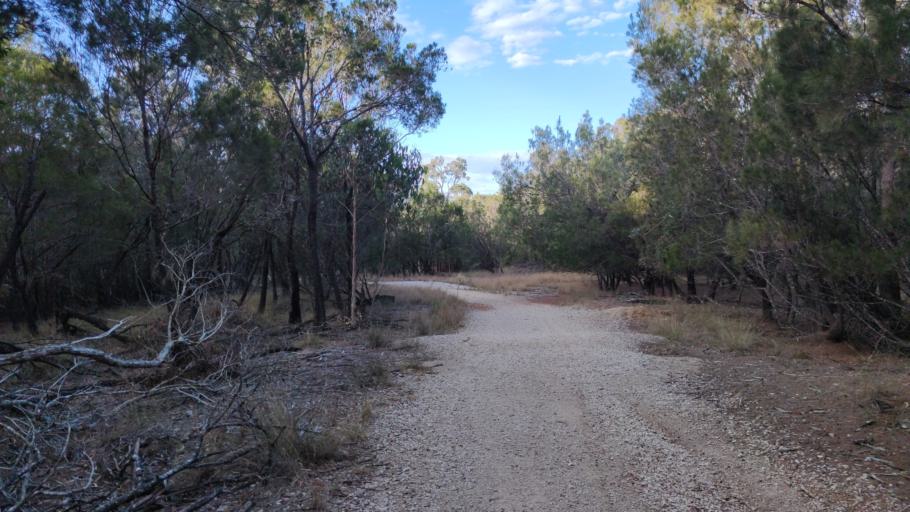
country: AU
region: Queensland
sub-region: Redland
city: Cleveland
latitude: -27.5508
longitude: 153.2433
